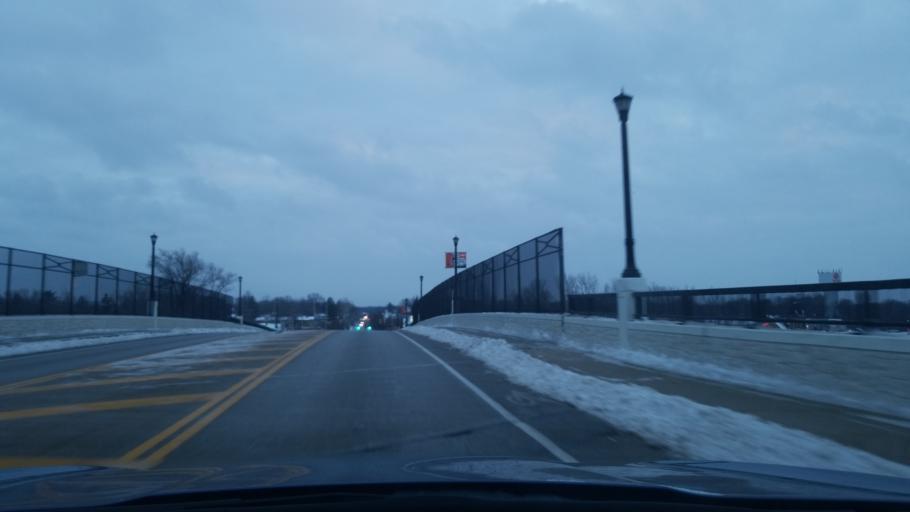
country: US
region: Ohio
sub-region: Cuyahoga County
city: Berea
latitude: 41.3827
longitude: -81.8531
